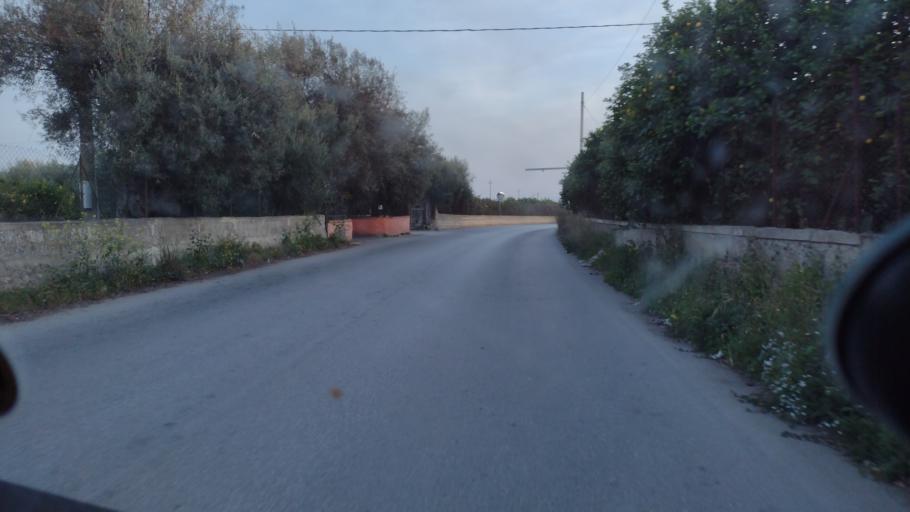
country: IT
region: Sicily
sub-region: Provincia di Siracusa
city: Avola
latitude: 36.8832
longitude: 15.1312
